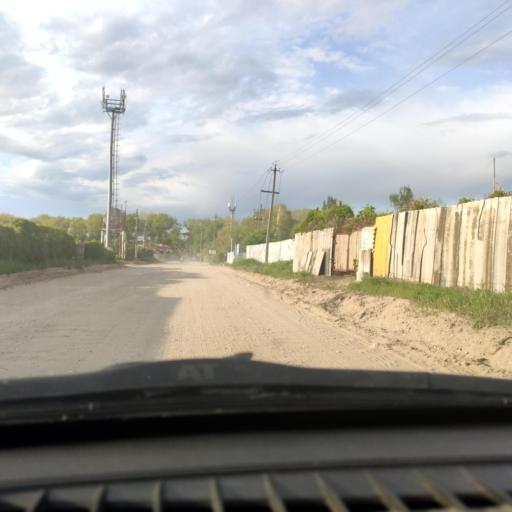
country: RU
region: Samara
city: Zhigulevsk
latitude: 53.4548
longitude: 49.5354
